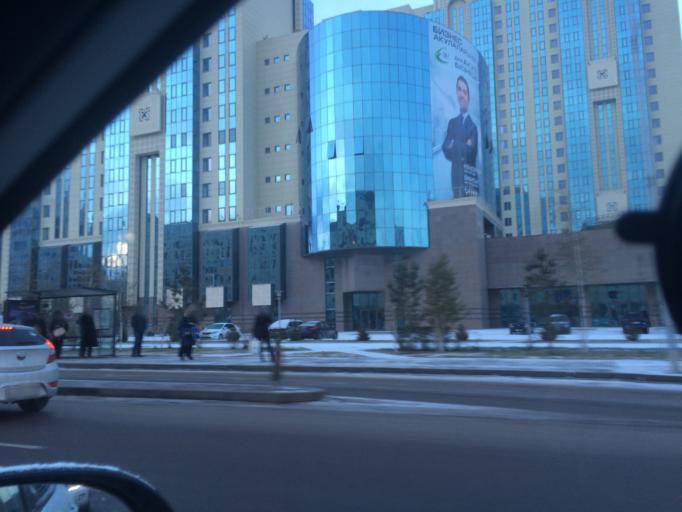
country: KZ
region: Astana Qalasy
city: Astana
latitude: 51.1621
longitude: 71.4100
